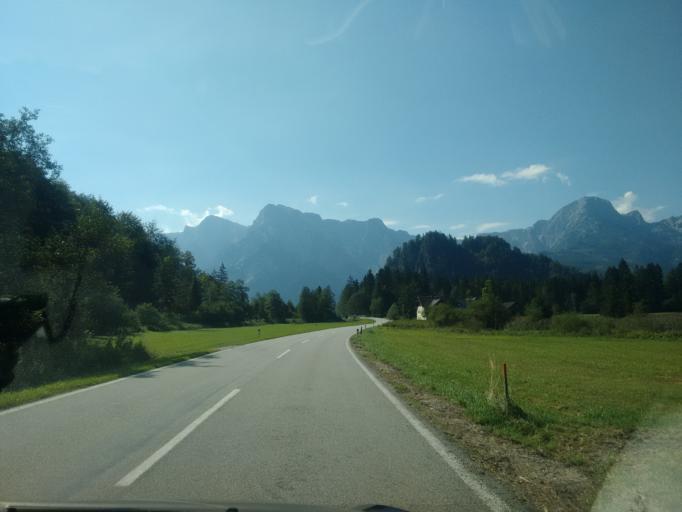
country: AT
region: Upper Austria
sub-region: Politischer Bezirk Gmunden
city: Gruenau im Almtal
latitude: 47.7692
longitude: 13.9567
